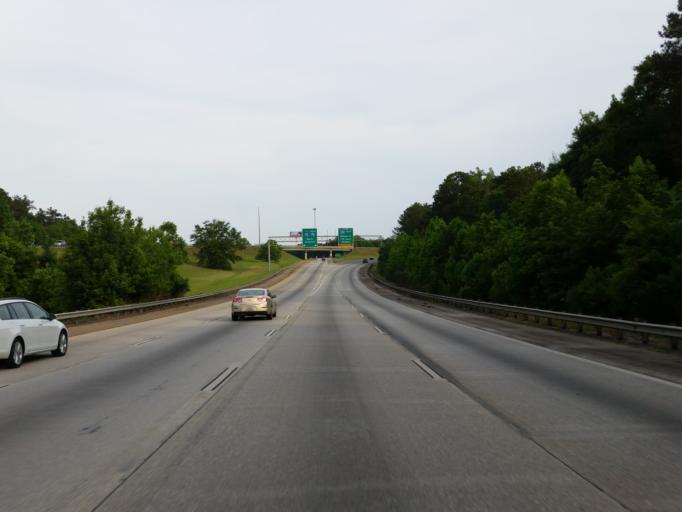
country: US
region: Georgia
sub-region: Monroe County
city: Forsyth
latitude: 32.9606
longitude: -83.8154
